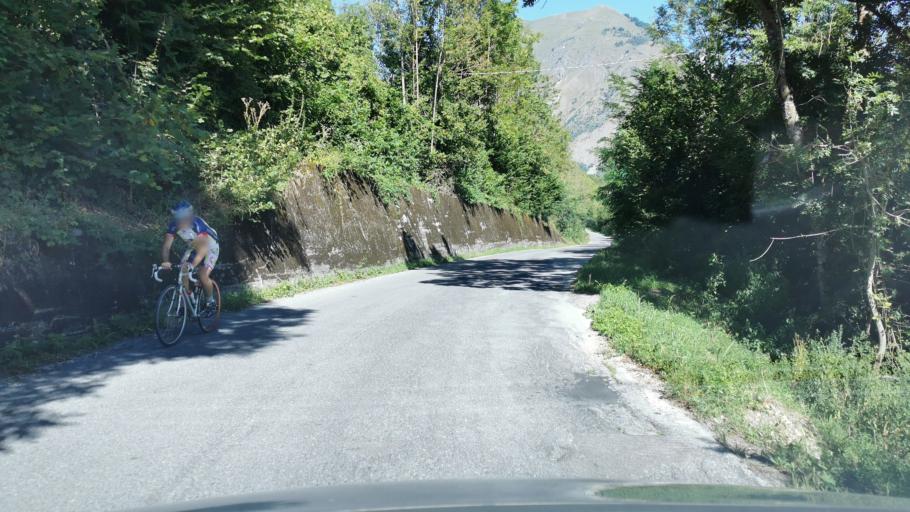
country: IT
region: Piedmont
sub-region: Provincia di Cuneo
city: Entracque
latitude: 44.2456
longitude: 7.3875
